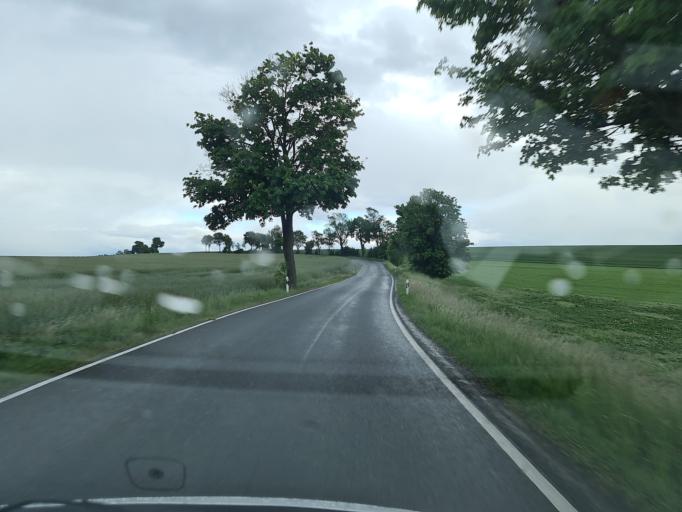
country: DE
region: Saxony
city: Muhltroff
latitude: 50.5006
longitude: 11.9210
